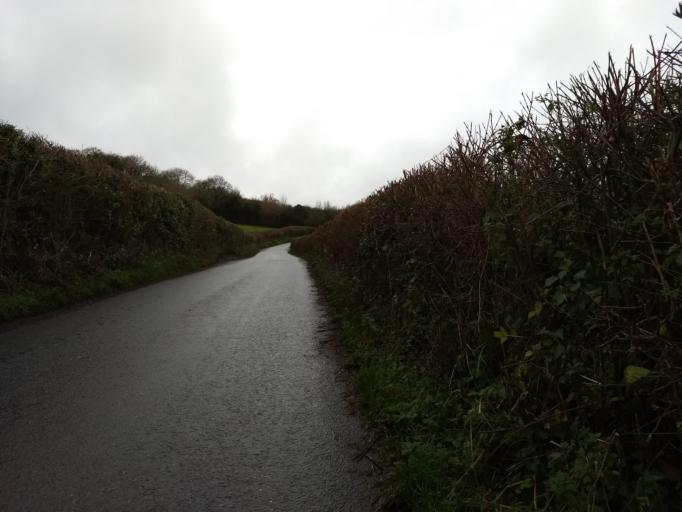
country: GB
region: England
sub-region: Isle of Wight
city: Newport
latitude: 50.6889
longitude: -1.2772
